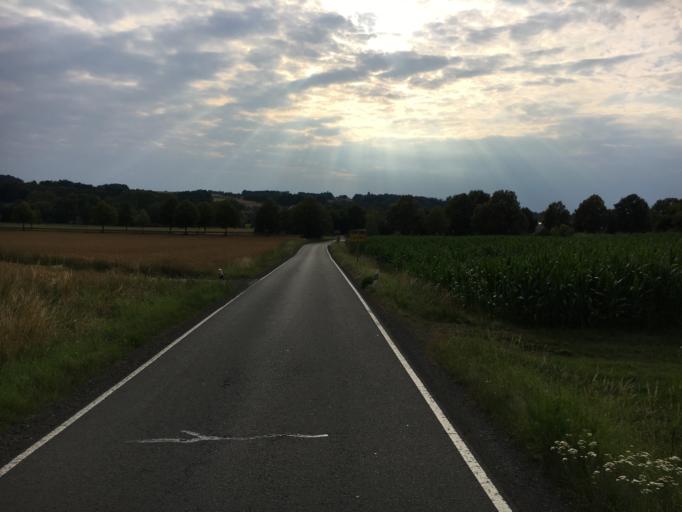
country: DE
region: Hesse
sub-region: Regierungsbezirk Kassel
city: Schrecksbach
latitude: 50.8520
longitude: 9.2951
